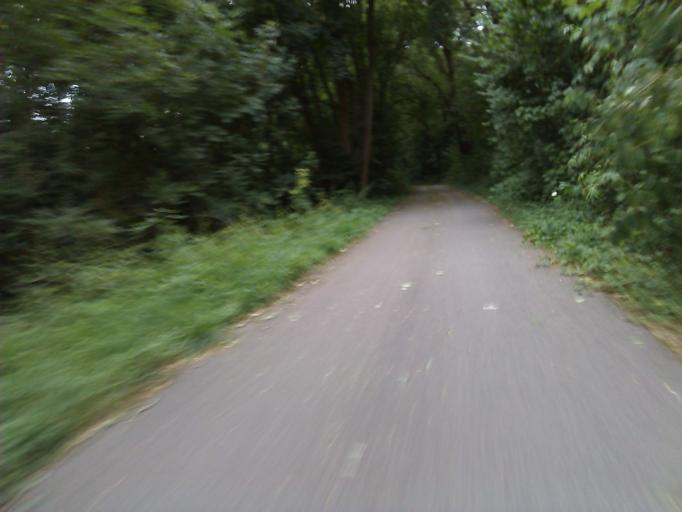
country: DE
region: Baden-Wuerttemberg
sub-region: Regierungsbezirk Stuttgart
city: Talheim
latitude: 49.1072
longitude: 9.1777
